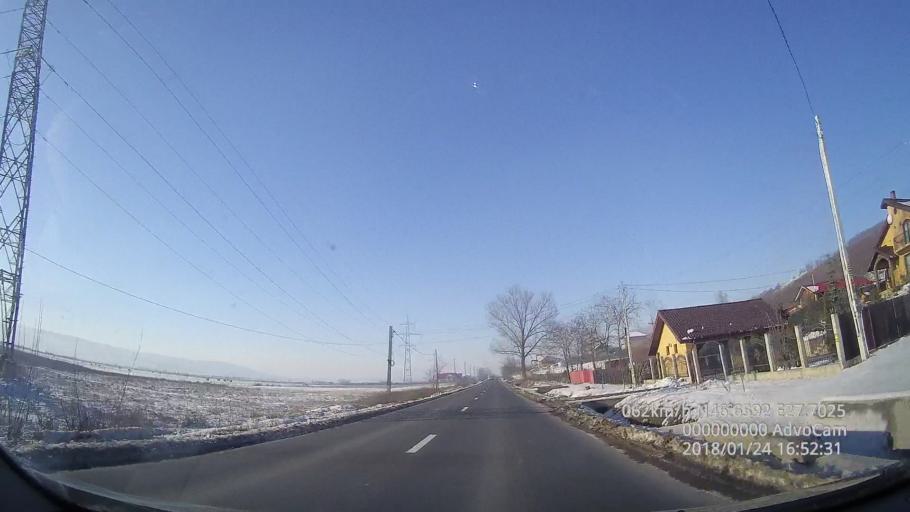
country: RO
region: Vaslui
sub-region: Municipiul Vaslui
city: Brodoc
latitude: 46.6595
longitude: 27.7020
